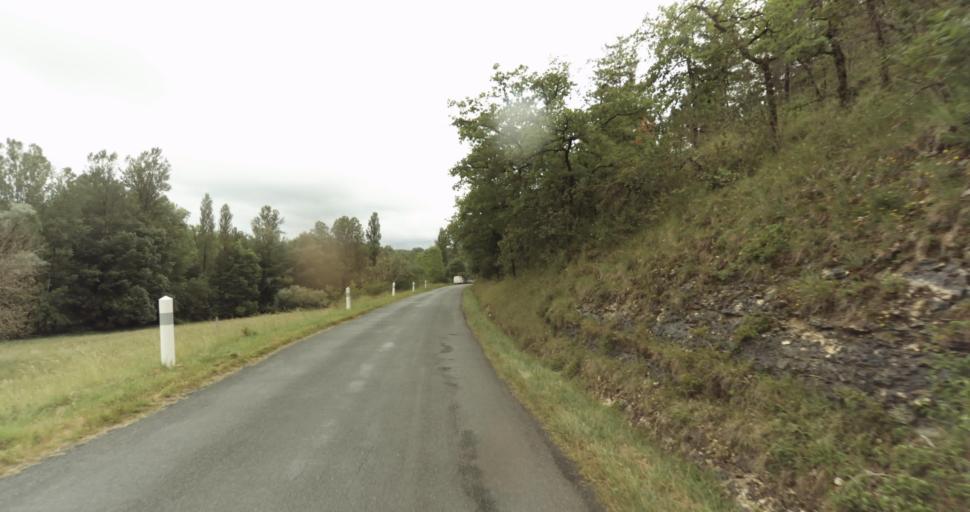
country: FR
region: Aquitaine
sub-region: Departement de la Dordogne
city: Beaumont-du-Perigord
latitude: 44.7540
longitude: 0.8753
